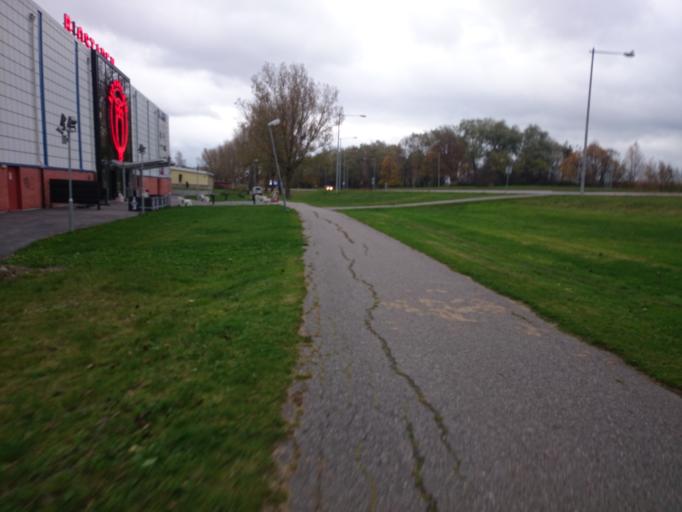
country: SE
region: Soedermanland
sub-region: Nykopings Kommun
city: Nykoping
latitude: 58.7494
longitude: 16.9884
